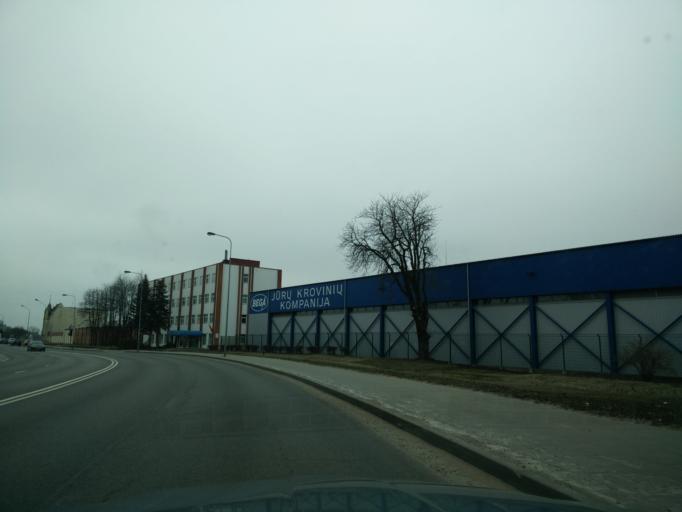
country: LT
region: Klaipedos apskritis
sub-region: Klaipeda
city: Klaipeda
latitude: 55.7004
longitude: 21.1355
